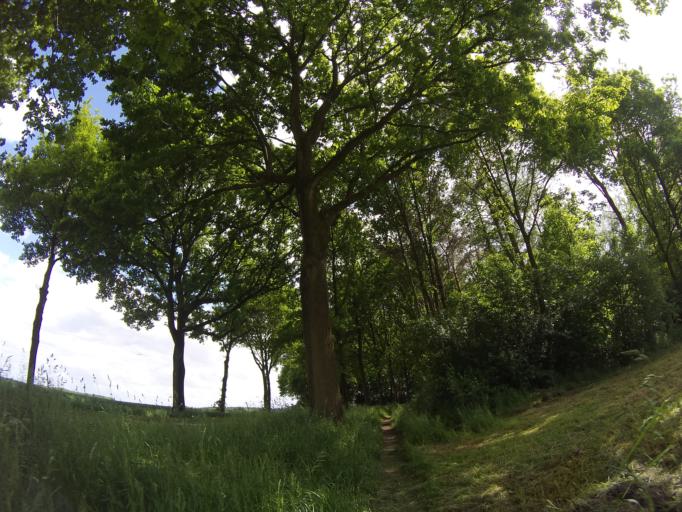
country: NL
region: Drenthe
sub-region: Gemeente Borger-Odoorn
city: Borger
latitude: 52.8795
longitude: 6.8703
